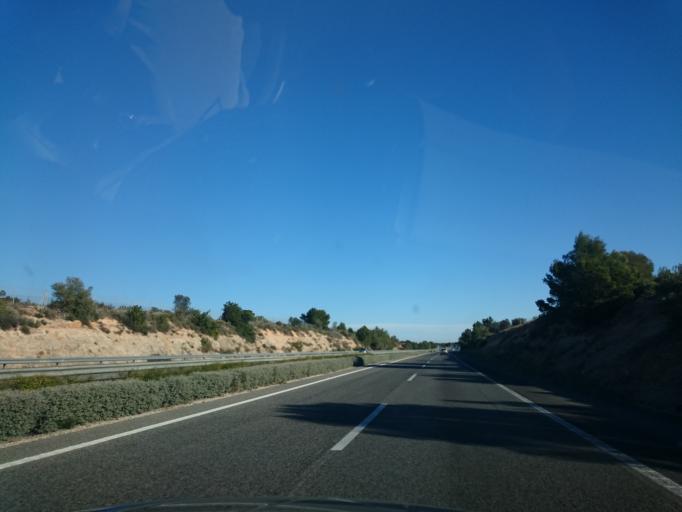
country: ES
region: Catalonia
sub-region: Provincia de Tarragona
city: l'Ametlla de Mar
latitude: 40.8703
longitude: 0.7818
